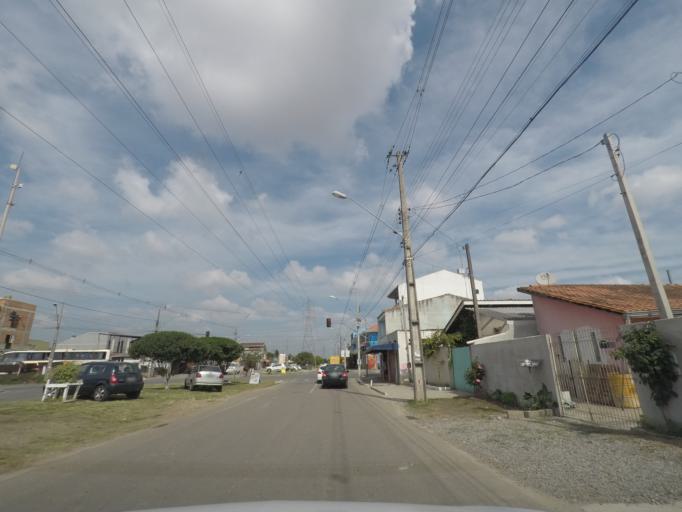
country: BR
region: Parana
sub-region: Pinhais
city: Pinhais
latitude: -25.4590
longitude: -49.1970
